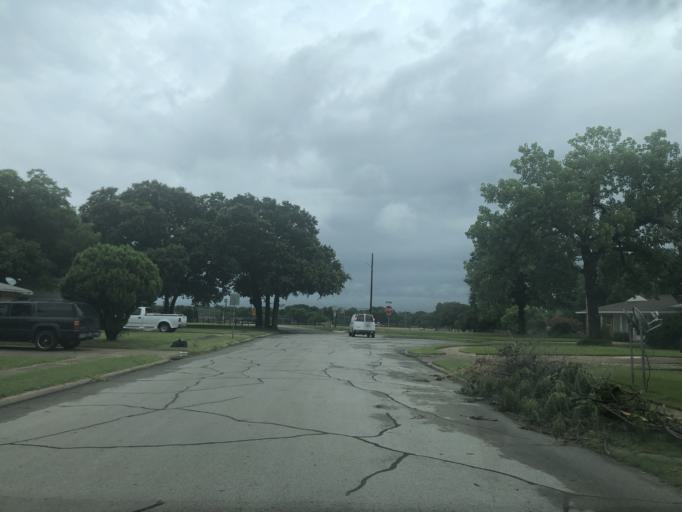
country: US
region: Texas
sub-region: Dallas County
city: Irving
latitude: 32.7968
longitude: -96.9439
